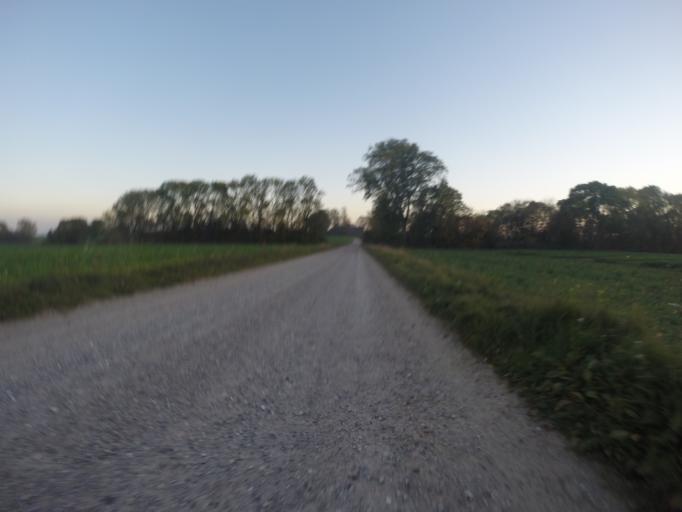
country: DK
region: Capital Region
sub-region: Hoje-Taastrup Kommune
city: Taastrup
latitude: 55.6768
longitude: 12.2940
